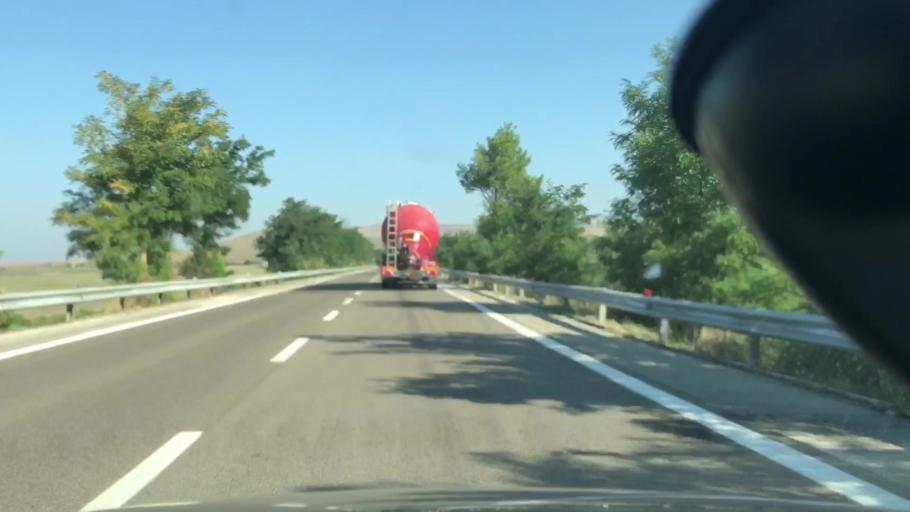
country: IT
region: Basilicate
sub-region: Provincia di Matera
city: Irsina
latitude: 40.8002
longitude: 16.2746
